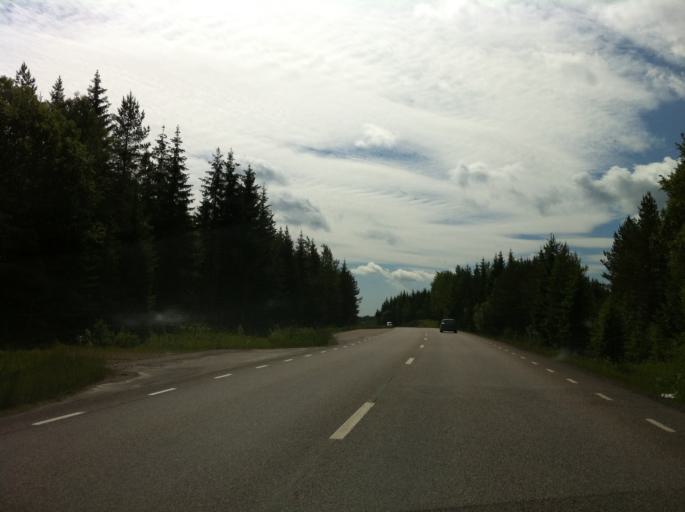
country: SE
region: Vaermland
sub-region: Saffle Kommun
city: Saeffle
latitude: 59.2325
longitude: 13.0010
